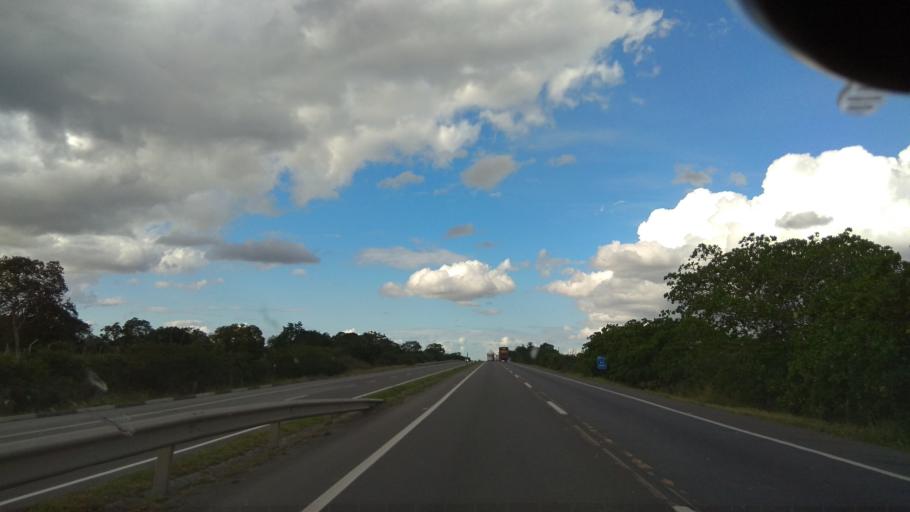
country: BR
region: Bahia
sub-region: Castro Alves
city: Castro Alves
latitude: -12.5641
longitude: -39.4802
